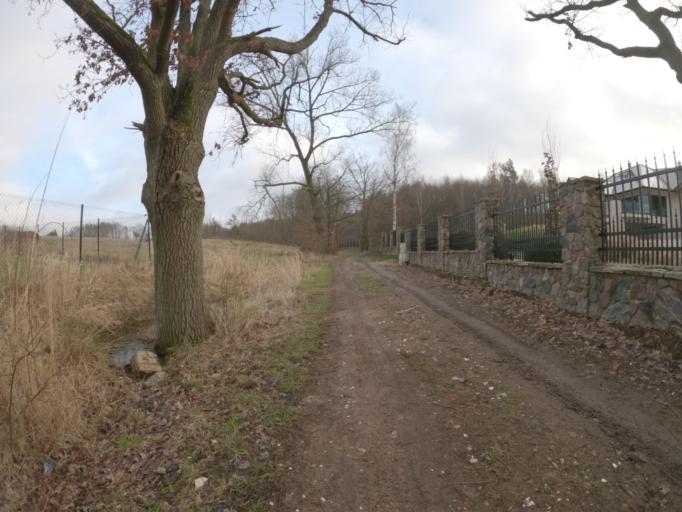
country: PL
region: West Pomeranian Voivodeship
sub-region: Koszalin
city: Koszalin
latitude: 54.2285
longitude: 16.2117
